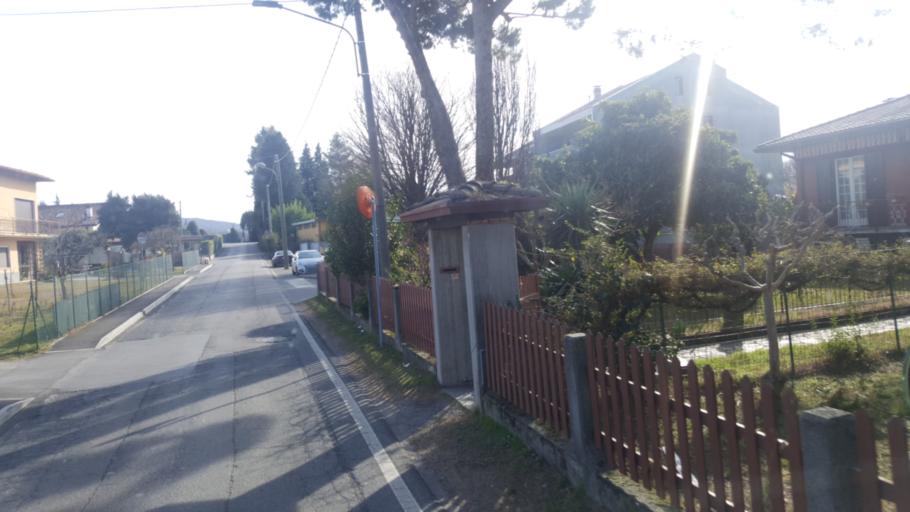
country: IT
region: Lombardy
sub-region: Provincia di Varese
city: Cadrezzate
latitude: 45.8011
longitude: 8.6456
